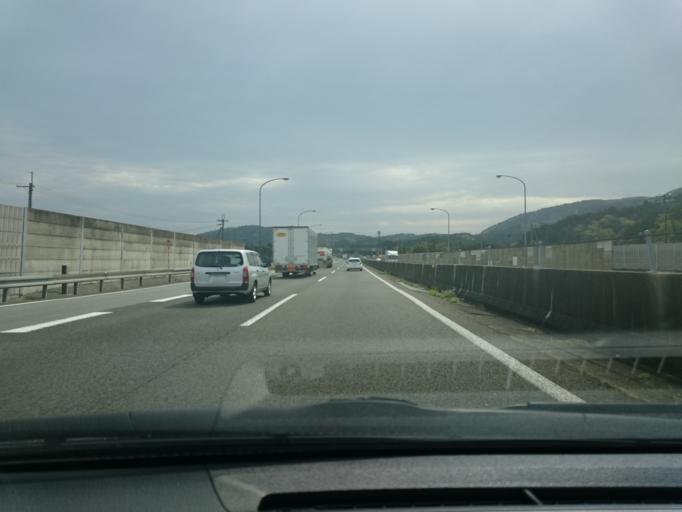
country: JP
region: Shiga Prefecture
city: Nagahama
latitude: 35.3326
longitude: 136.3879
